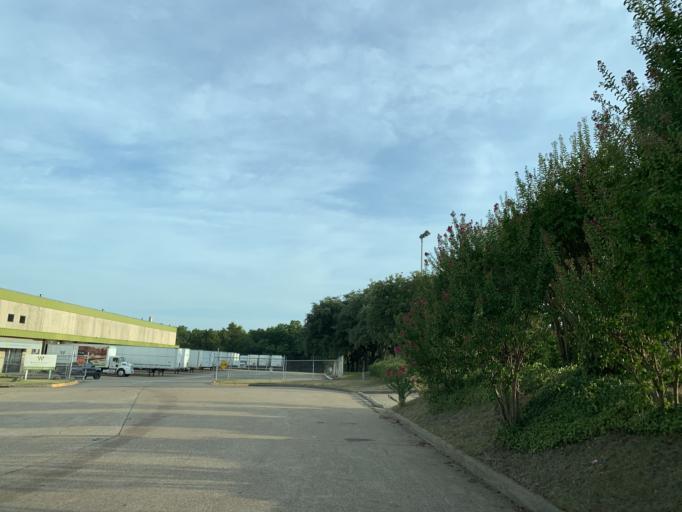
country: US
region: Texas
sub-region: Dallas County
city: Cockrell Hill
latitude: 32.6997
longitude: -96.9017
